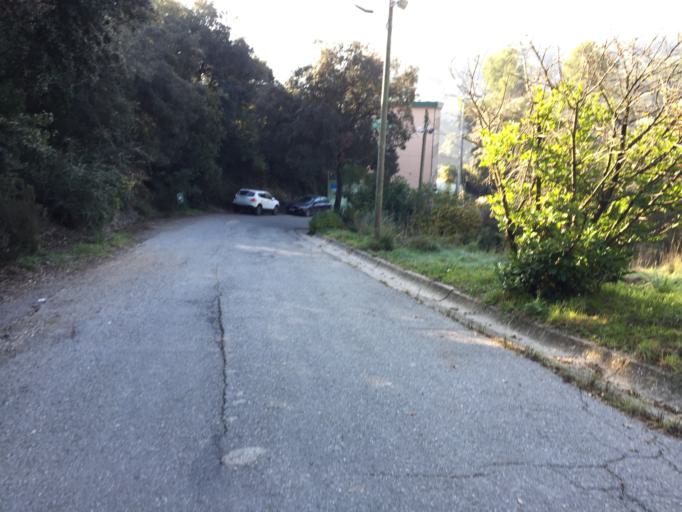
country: ES
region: Catalonia
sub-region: Provincia de Barcelona
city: Sant Just Desvern
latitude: 41.4220
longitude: 2.0976
